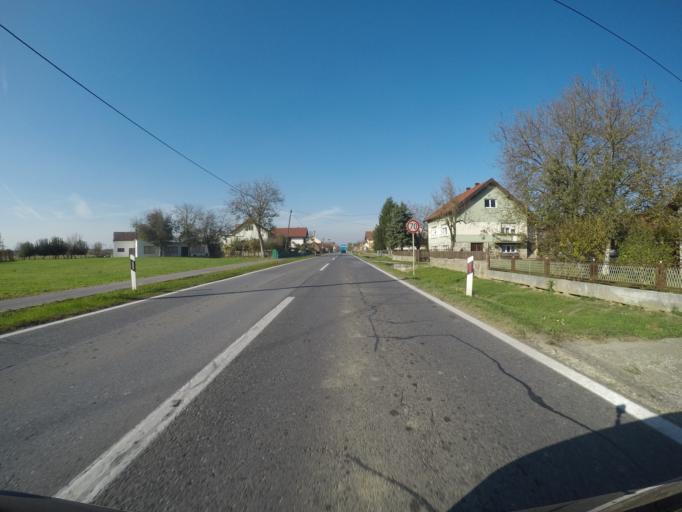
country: HR
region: Bjelovarsko-Bilogorska
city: Predavac
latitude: 45.9249
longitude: 16.7878
